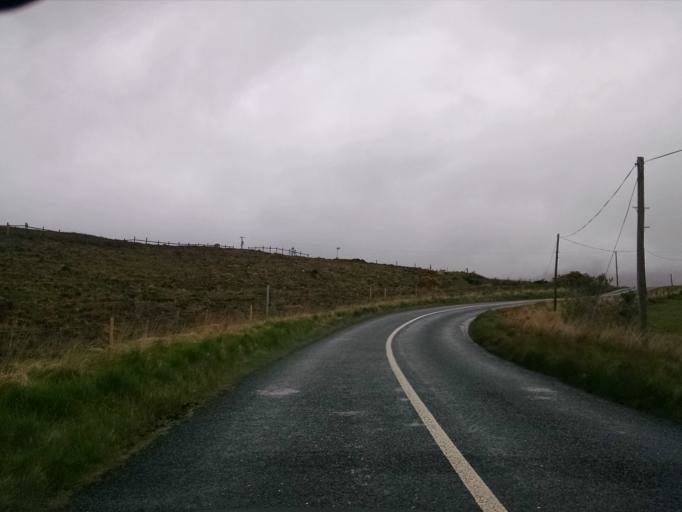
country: IE
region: Connaught
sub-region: County Galway
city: Clifden
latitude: 53.4873
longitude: -9.7400
